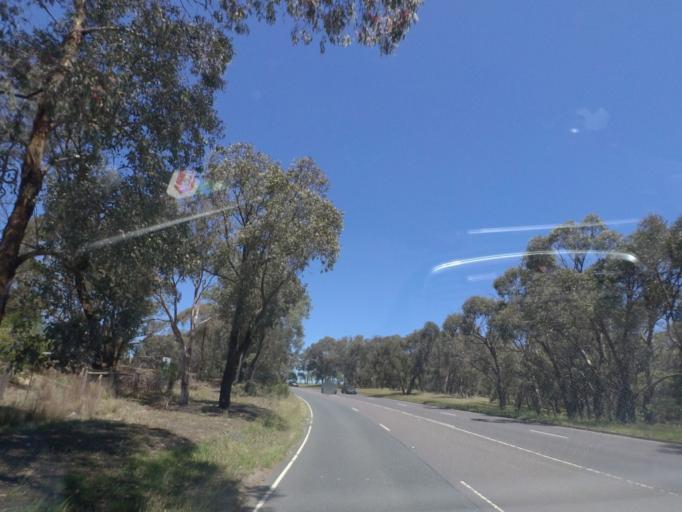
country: AU
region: Victoria
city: Plenty
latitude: -37.6499
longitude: 145.1128
